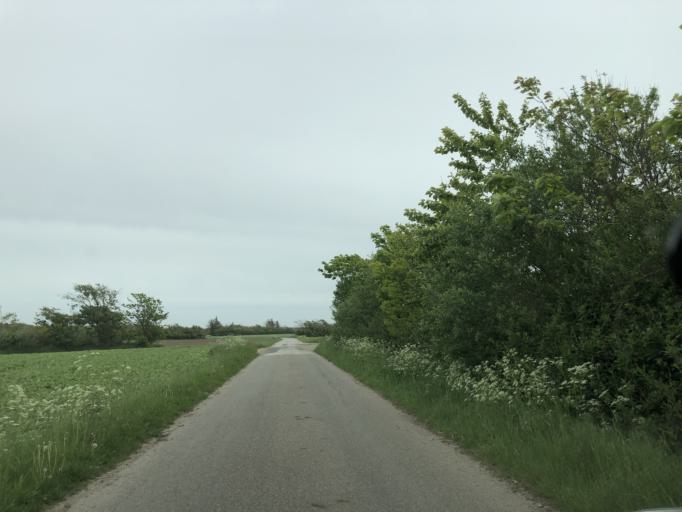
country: DK
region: Central Jutland
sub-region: Holstebro Kommune
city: Ulfborg
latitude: 56.2755
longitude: 8.1765
